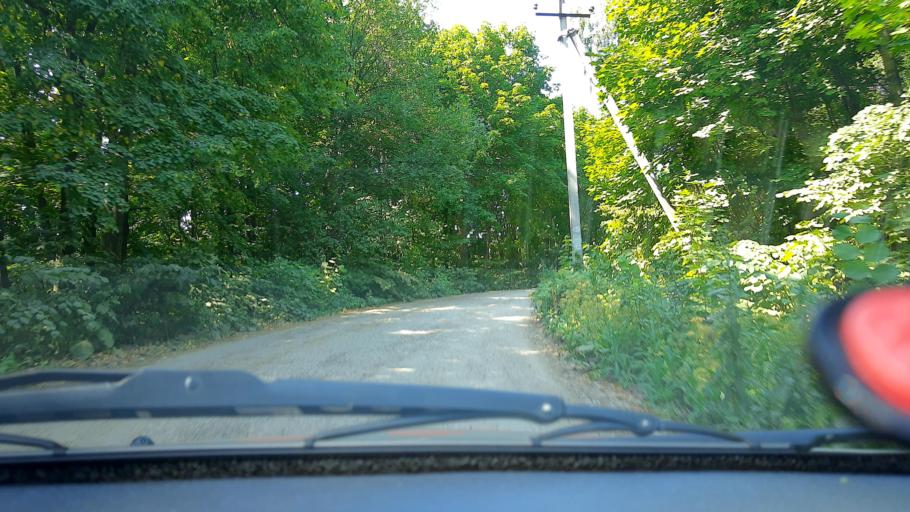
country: RU
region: Bashkortostan
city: Karmaskaly
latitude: 54.3870
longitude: 55.9028
